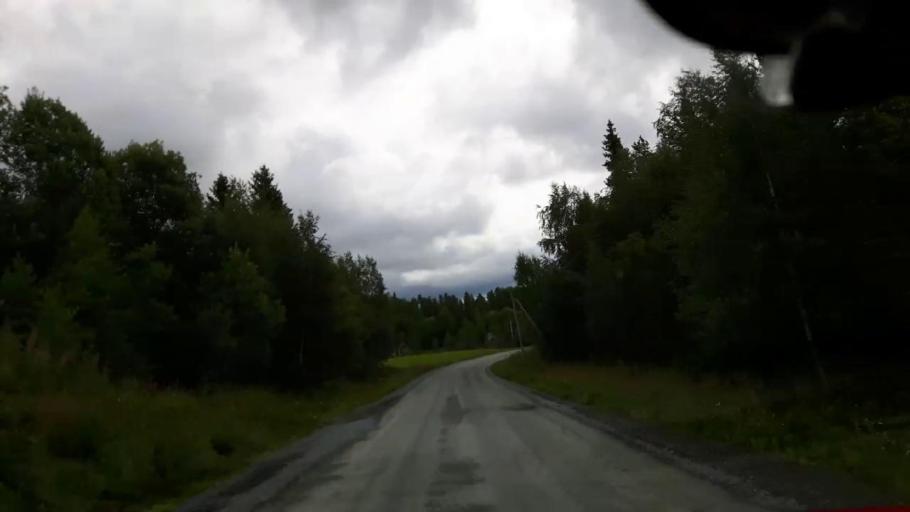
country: SE
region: Jaemtland
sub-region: Krokoms Kommun
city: Krokom
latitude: 63.5733
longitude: 14.2392
